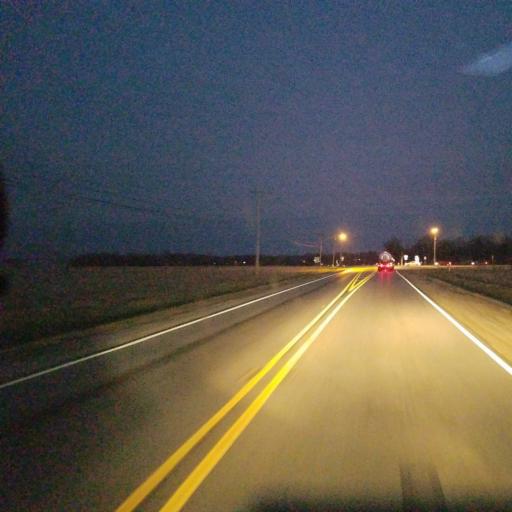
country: US
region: Illinois
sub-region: Peoria County
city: Bellevue
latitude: 40.6927
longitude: -89.6940
